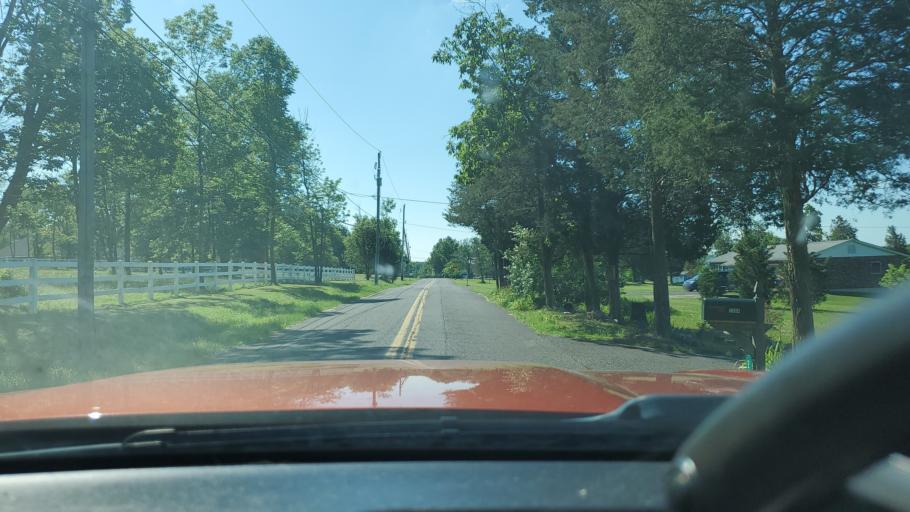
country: US
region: Pennsylvania
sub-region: Montgomery County
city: Woxall
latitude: 40.3125
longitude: -75.5192
